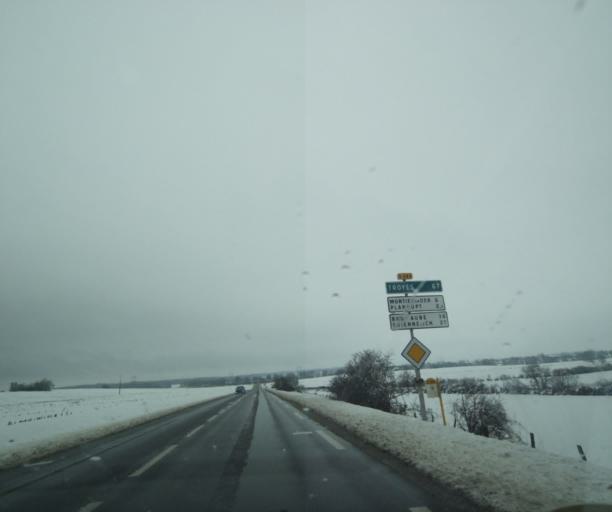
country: FR
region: Champagne-Ardenne
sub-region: Departement de la Haute-Marne
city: Montier-en-Der
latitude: 48.5156
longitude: 4.8071
